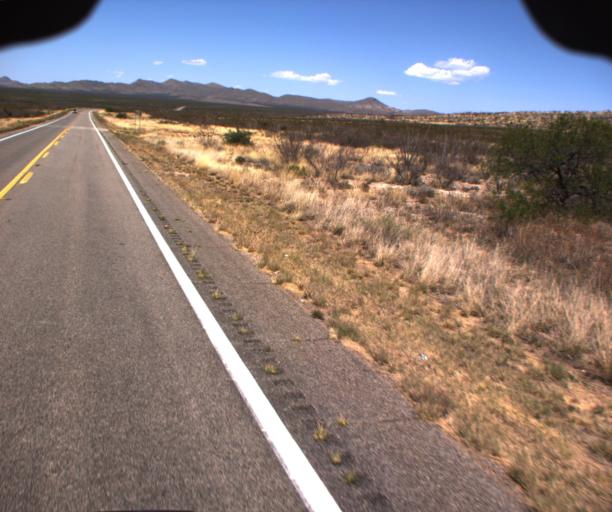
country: US
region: Arizona
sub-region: Cochise County
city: Tombstone
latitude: 31.5954
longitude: -110.0448
